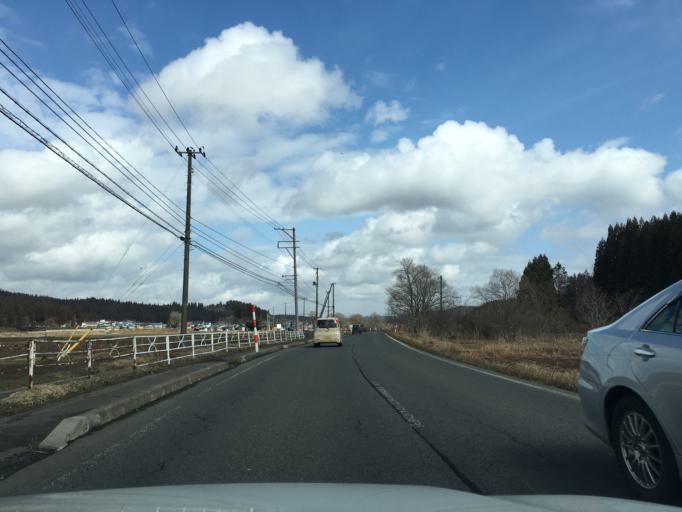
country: JP
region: Akita
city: Takanosu
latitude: 40.0379
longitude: 140.2779
